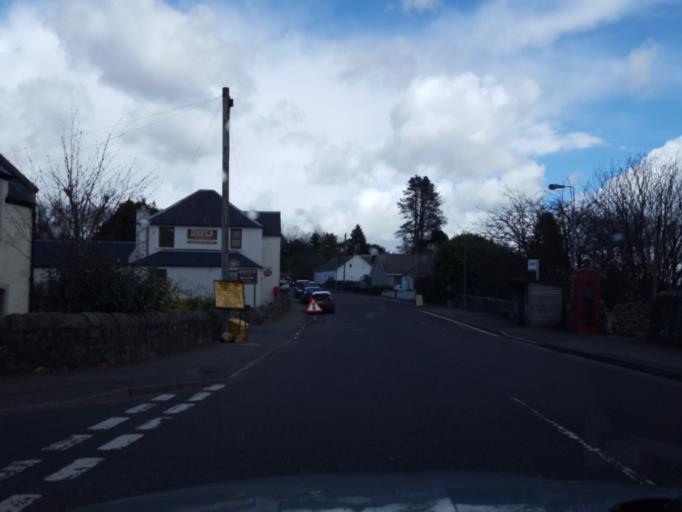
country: GB
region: Scotland
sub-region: Clackmannanshire
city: Dollar
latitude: 56.1888
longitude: -3.6116
